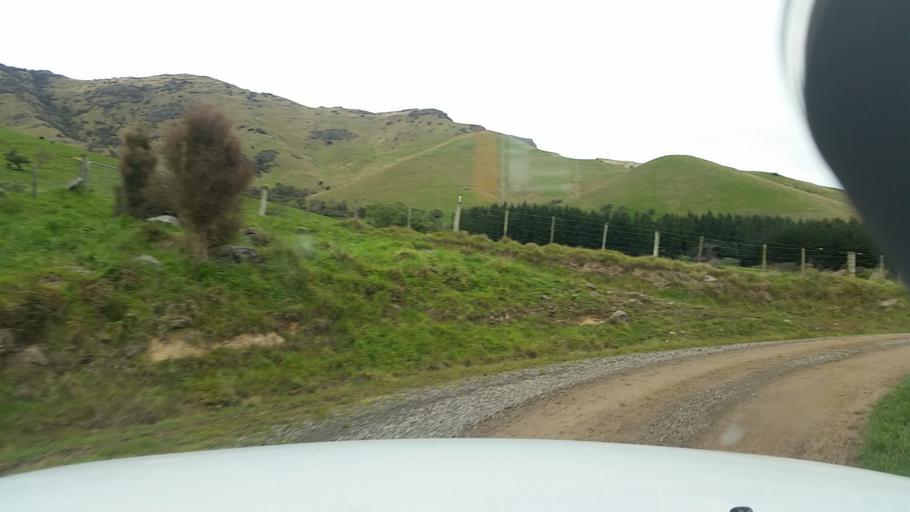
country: NZ
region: Canterbury
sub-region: Christchurch City
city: Christchurch
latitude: -43.6477
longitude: 172.8422
